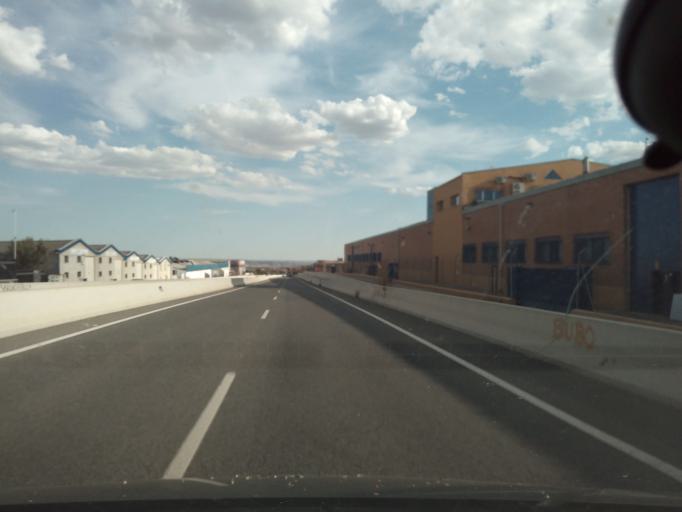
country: ES
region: Madrid
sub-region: Provincia de Madrid
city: Ajalvir
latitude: 40.5120
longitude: -3.4805
